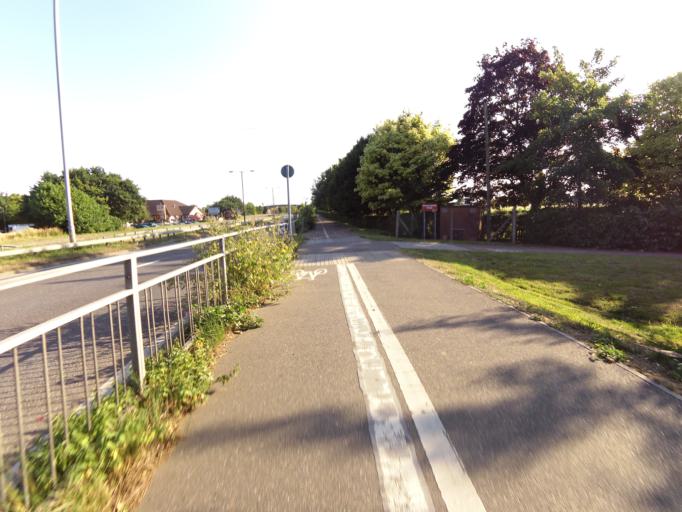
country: GB
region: England
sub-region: Essex
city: Chelmsford
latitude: 51.7414
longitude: 0.4984
